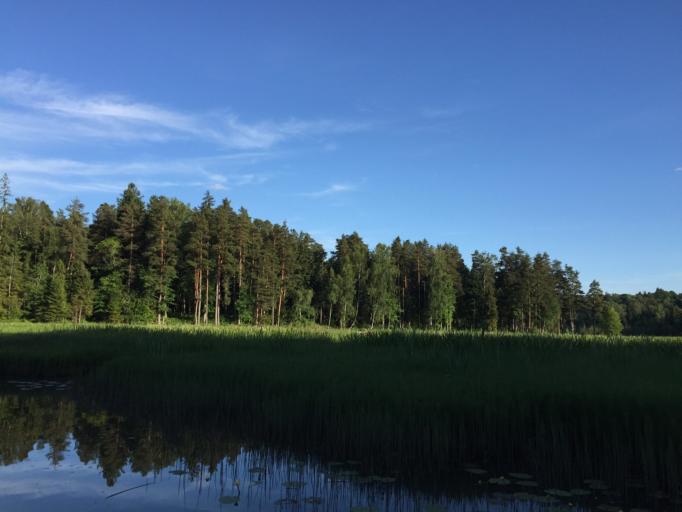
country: LV
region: Aizpute
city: Aizpute
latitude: 56.7250
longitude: 21.7408
